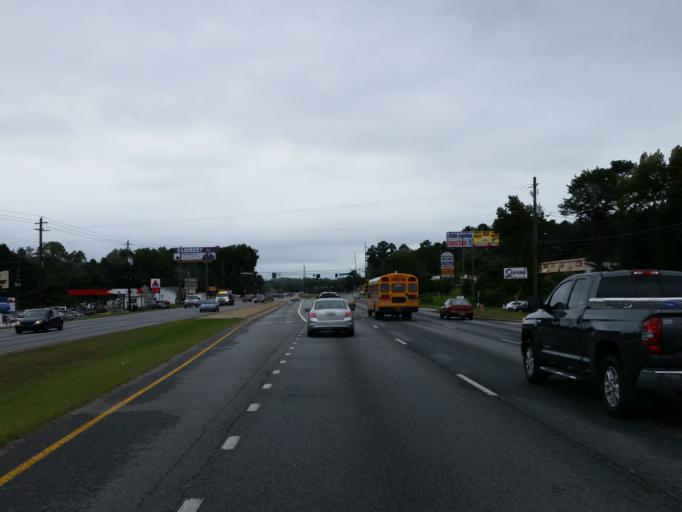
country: US
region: Georgia
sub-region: Clayton County
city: Jonesboro
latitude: 33.5530
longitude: -84.3704
